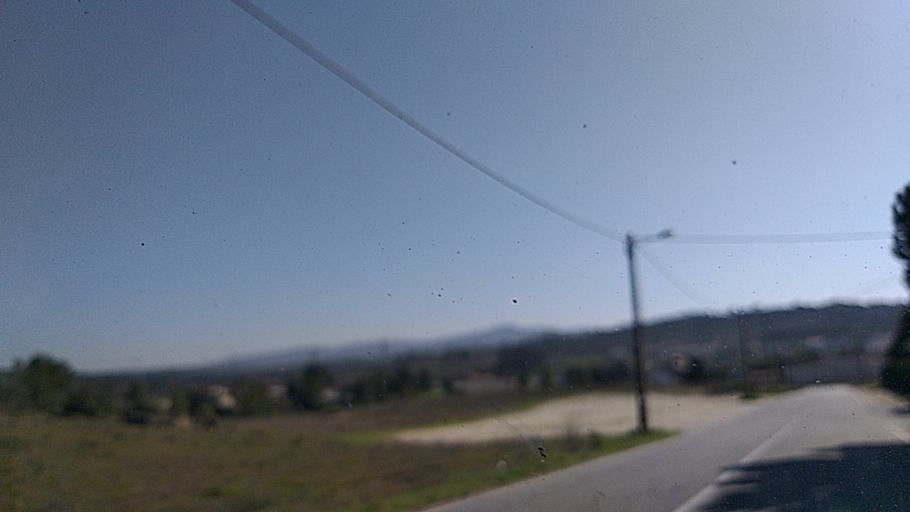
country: PT
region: Guarda
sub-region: Celorico da Beira
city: Celorico da Beira
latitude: 40.6700
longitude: -7.3878
